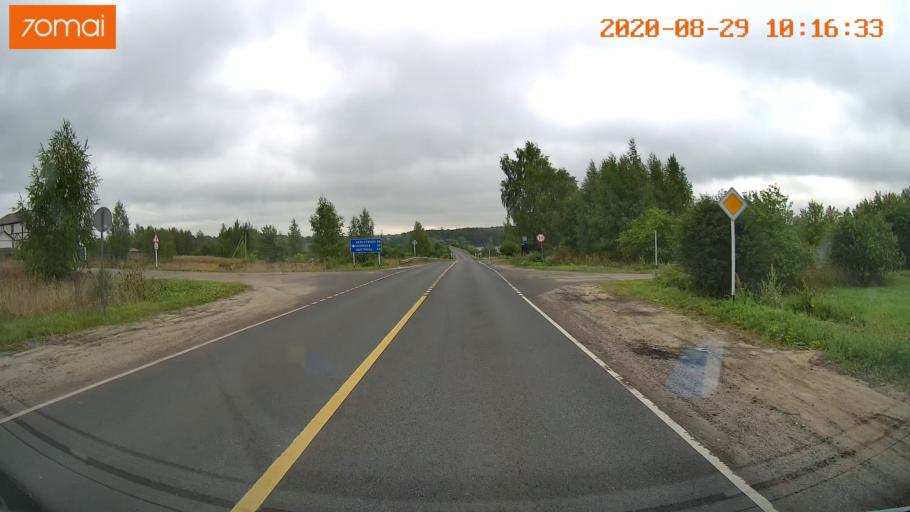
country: RU
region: Ivanovo
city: Yur'yevets
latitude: 57.3377
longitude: 42.7941
